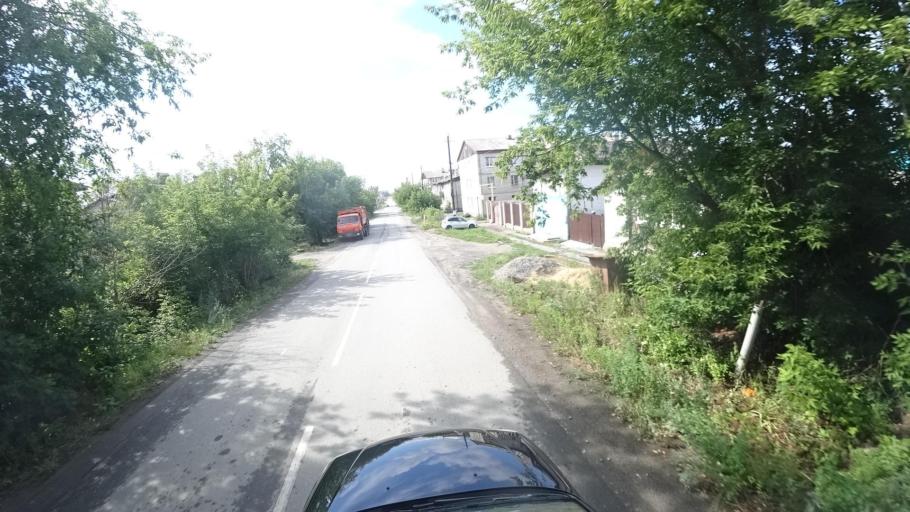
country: RU
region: Sverdlovsk
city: Kamyshlov
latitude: 56.8367
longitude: 62.7161
